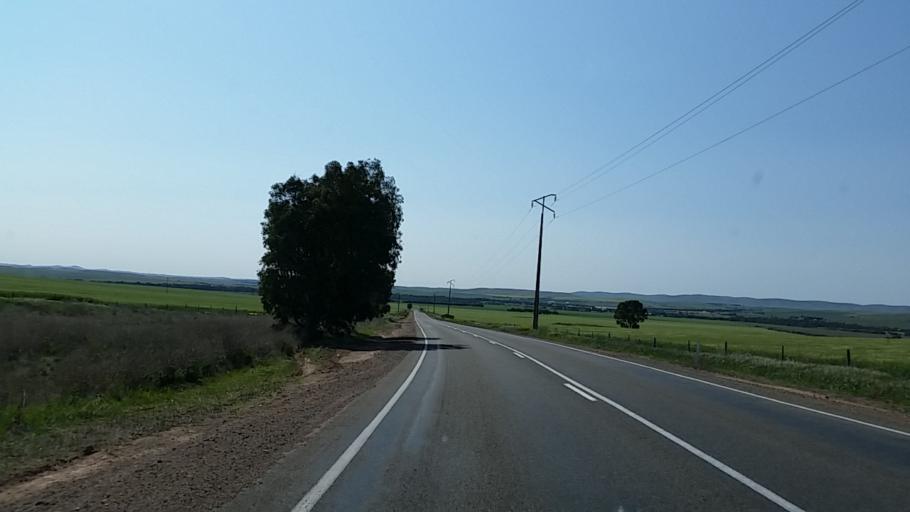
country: AU
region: South Australia
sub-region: Port Pirie City and Dists
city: Crystal Brook
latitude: -33.2776
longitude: 138.2973
